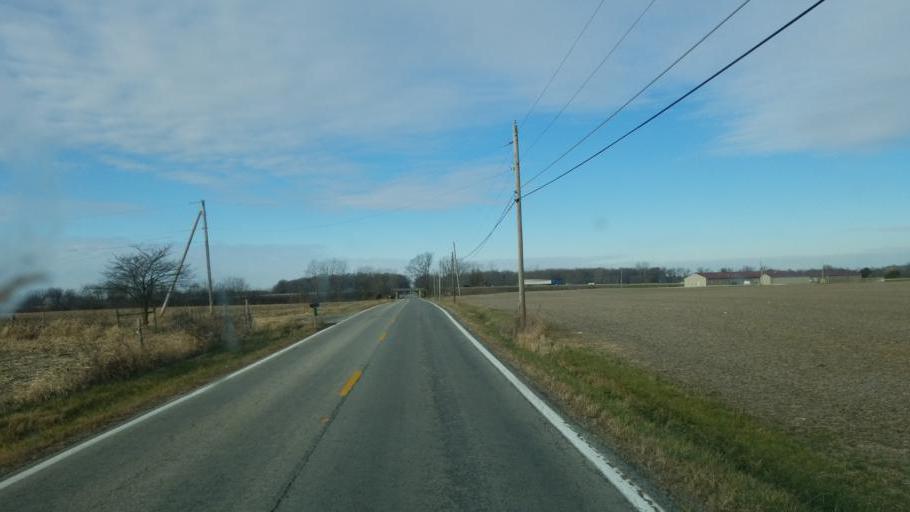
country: US
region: Ohio
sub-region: Marion County
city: Marion
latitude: 40.5495
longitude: -83.0695
